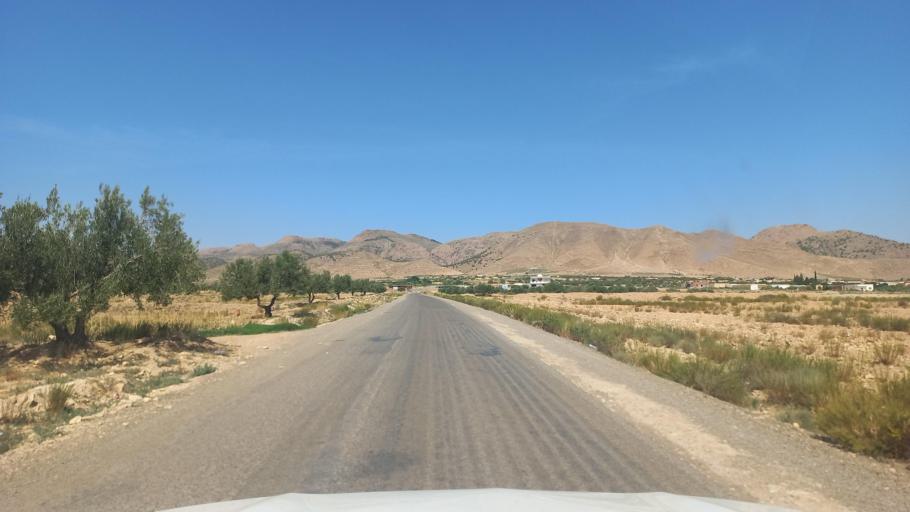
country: TN
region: Al Qasrayn
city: Sbiba
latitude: 35.4398
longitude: 9.0764
